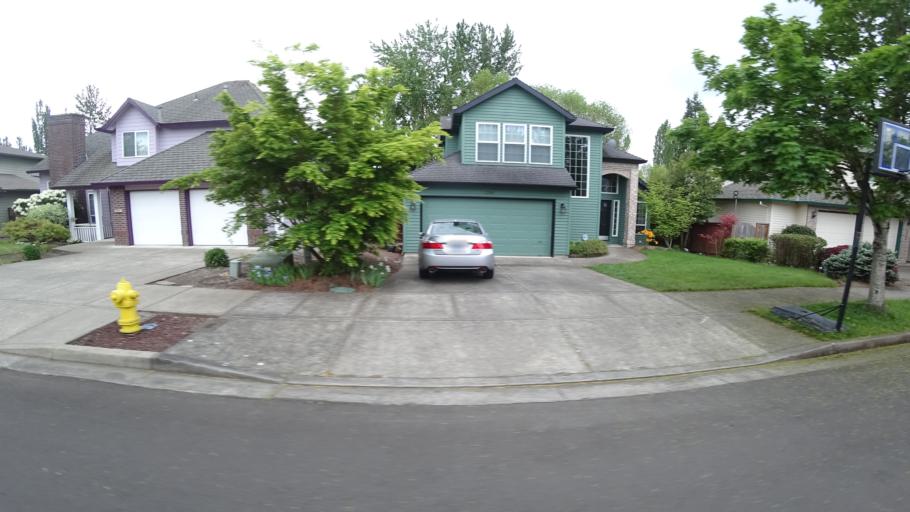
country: US
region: Oregon
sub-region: Washington County
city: Hillsboro
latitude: 45.5472
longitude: -122.9702
